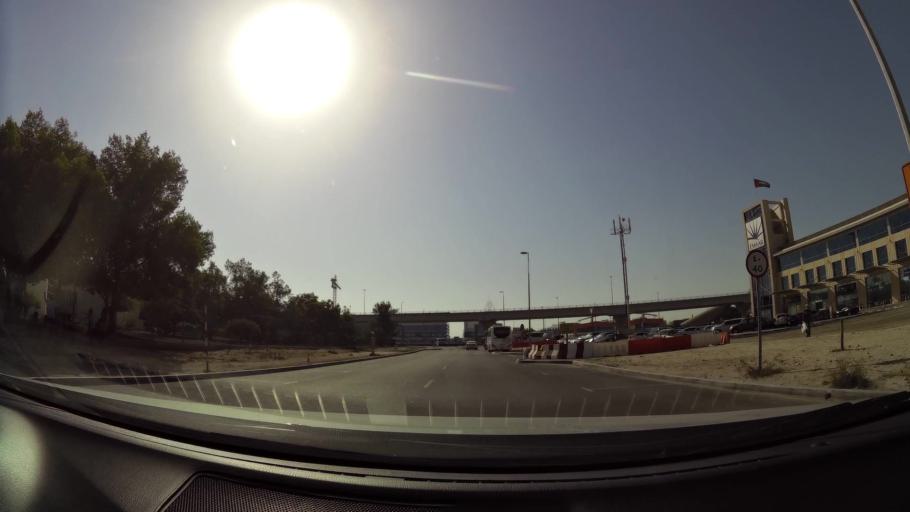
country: AE
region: Dubai
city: Dubai
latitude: 25.1250
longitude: 55.2076
